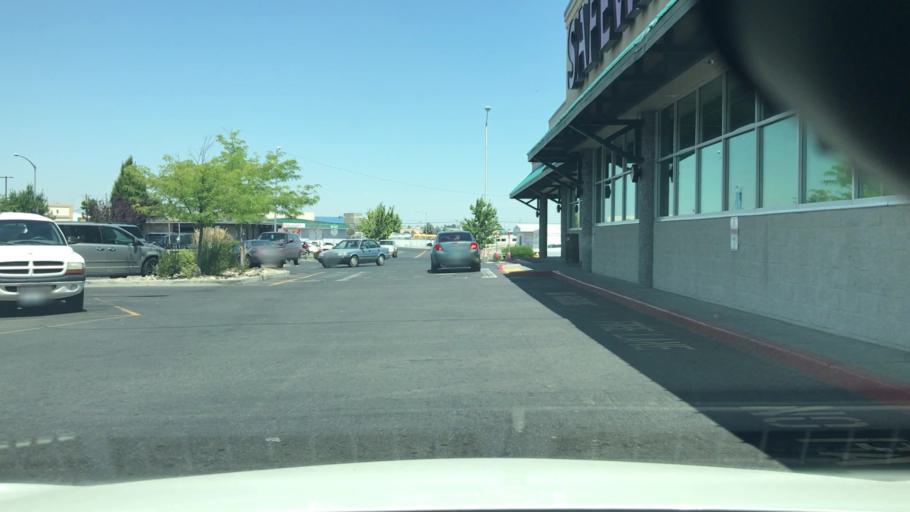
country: US
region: Washington
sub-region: Grant County
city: Moses Lake
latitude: 47.1304
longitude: -119.2687
